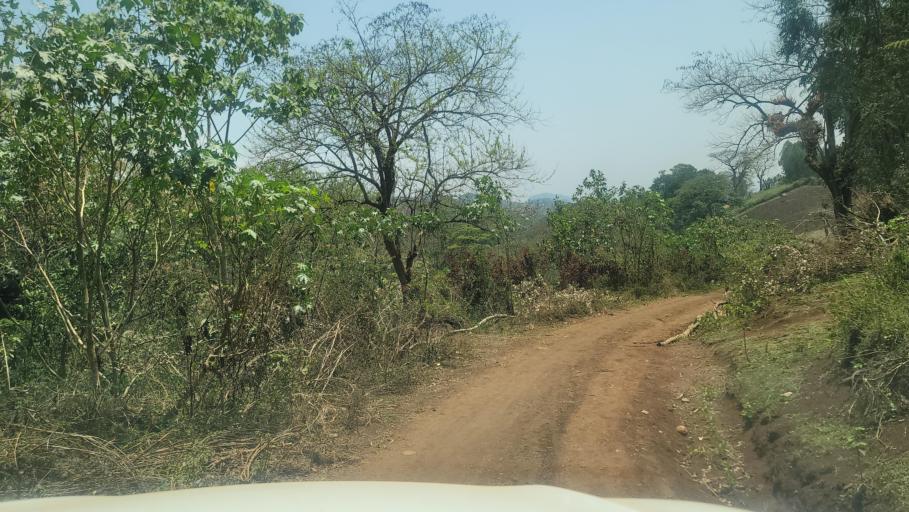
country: ET
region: Southern Nations, Nationalities, and People's Region
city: Bonga
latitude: 7.5286
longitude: 36.1951
